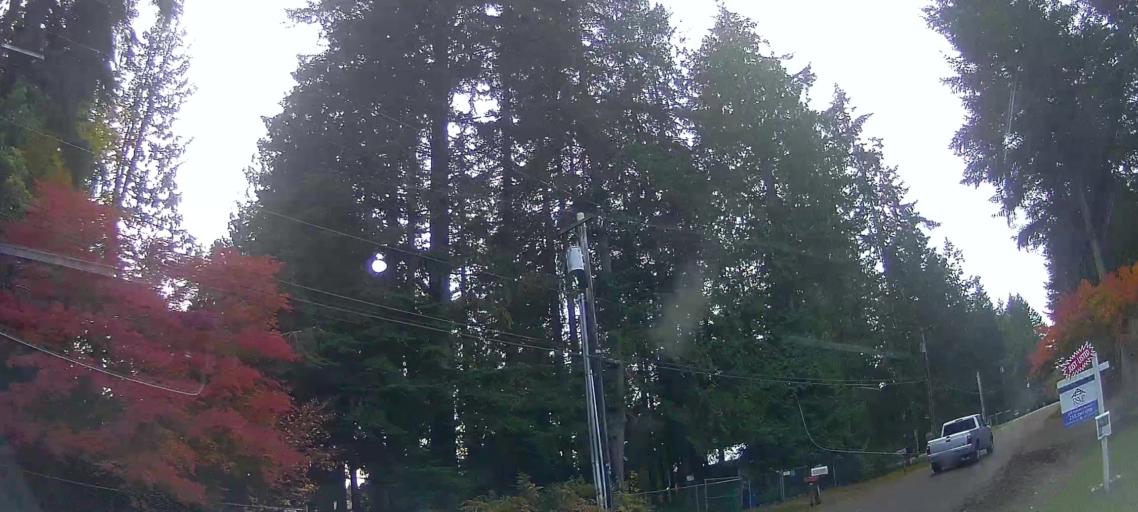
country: US
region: Washington
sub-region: Snohomish County
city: Stanwood
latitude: 48.2840
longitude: -122.3442
